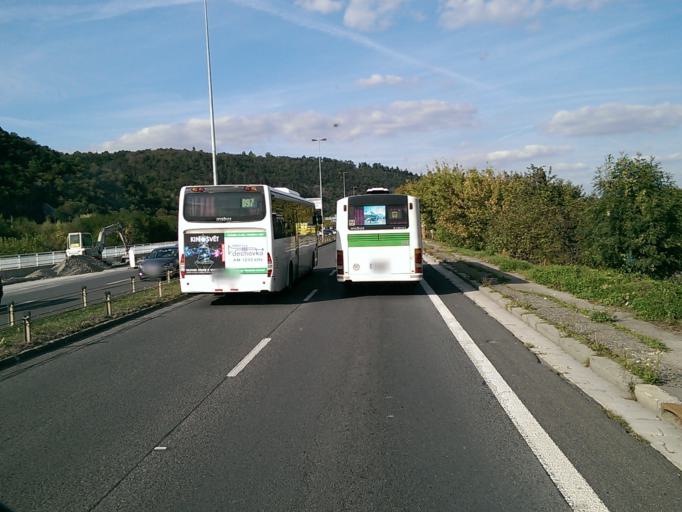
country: CZ
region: Praha
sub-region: Praha 12
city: Modrany
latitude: 50.0181
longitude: 14.3942
